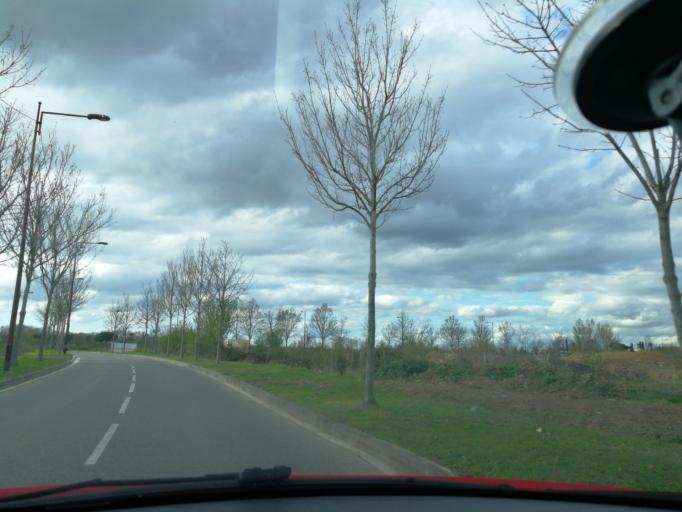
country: FR
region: Midi-Pyrenees
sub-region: Departement de la Haute-Garonne
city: Blagnac
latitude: 43.6327
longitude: 1.4110
